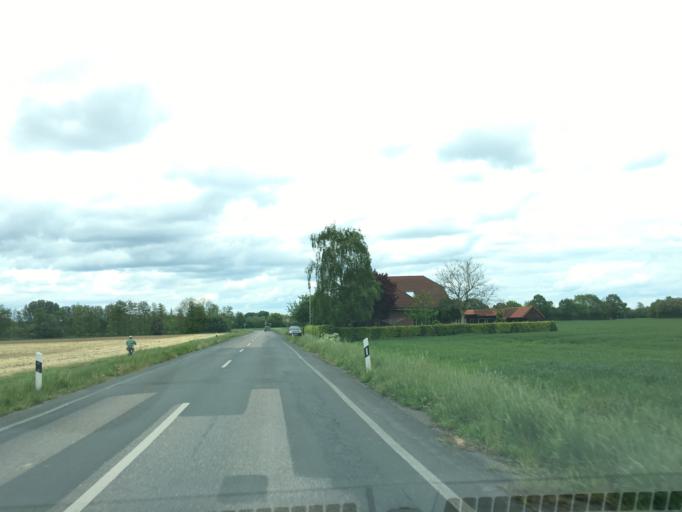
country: DE
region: North Rhine-Westphalia
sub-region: Regierungsbezirk Munster
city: Havixbeck
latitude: 51.9528
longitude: 7.5129
